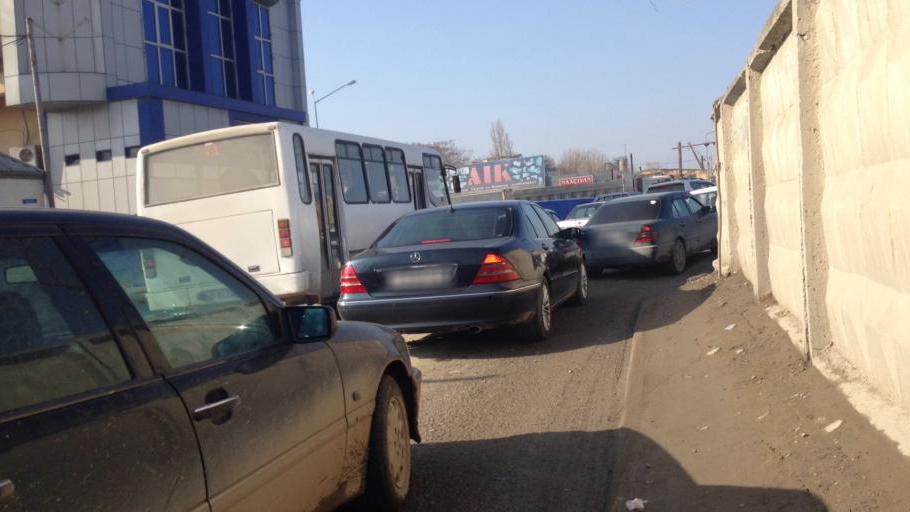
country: AZ
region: Baki
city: Binagadi
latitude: 40.4404
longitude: 49.8455
